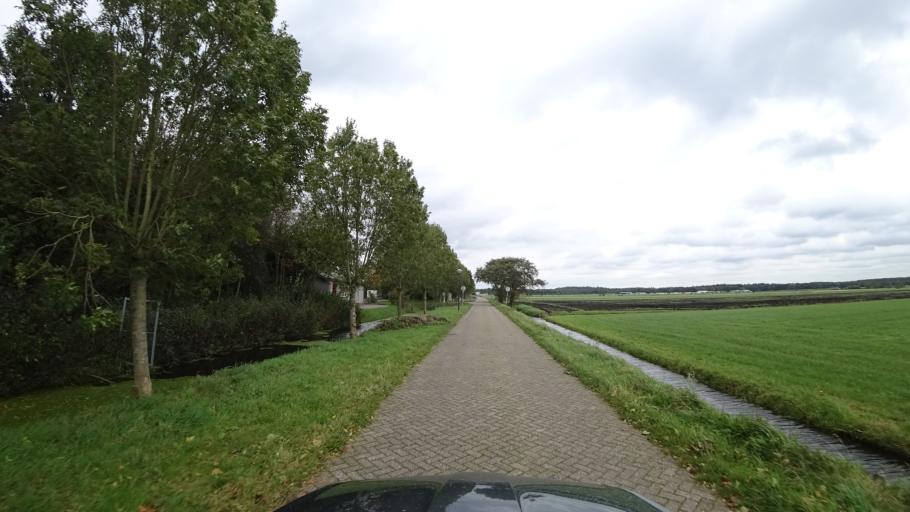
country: NL
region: North Holland
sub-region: Gemeente Wijdemeren
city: Nieuw-Loosdrecht
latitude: 52.1895
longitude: 5.1340
